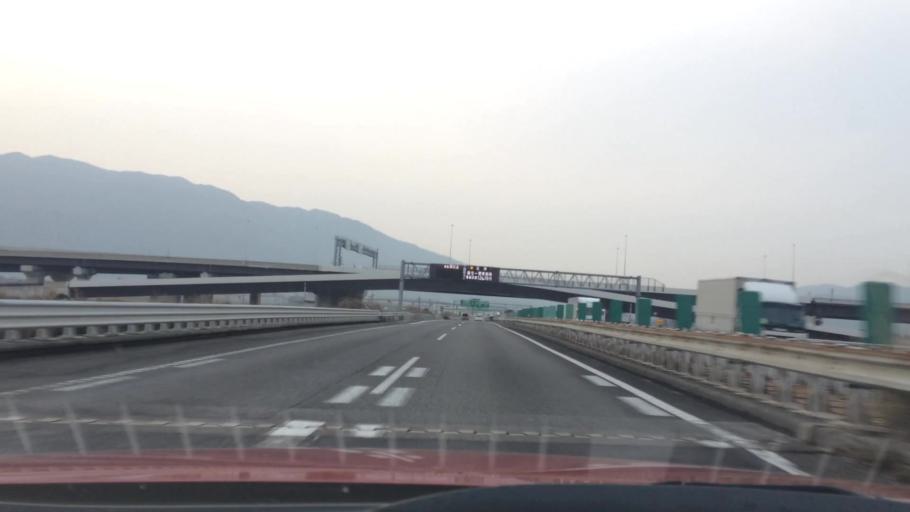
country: JP
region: Gifu
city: Ogaki
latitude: 35.3177
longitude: 136.5825
